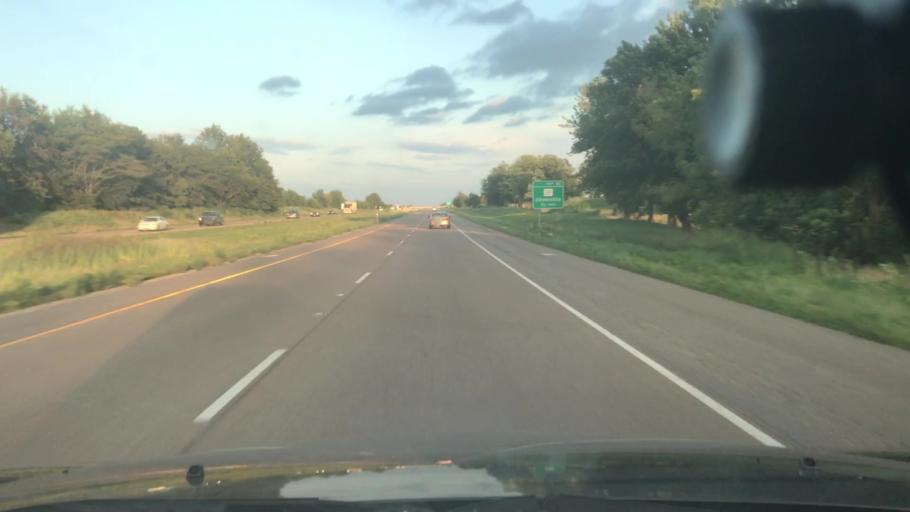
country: US
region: Illinois
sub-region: Washington County
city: Okawville
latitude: 38.4471
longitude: -89.5443
